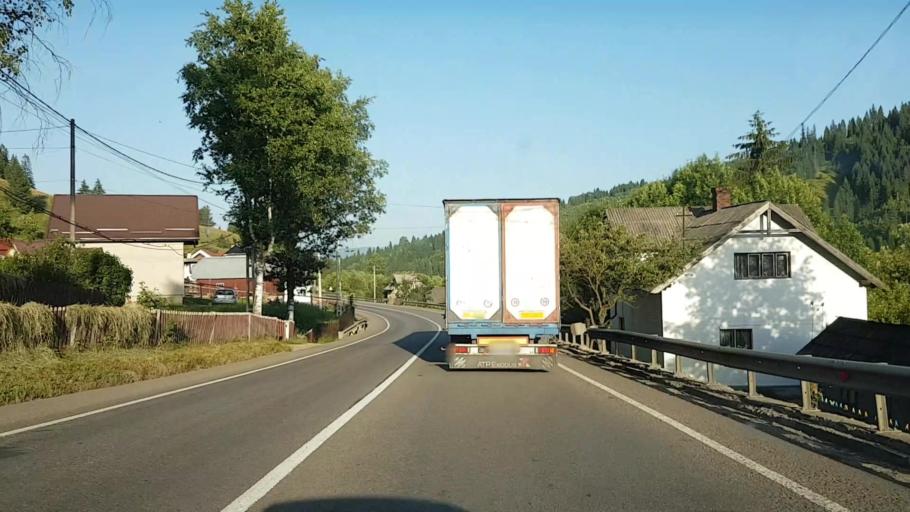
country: RO
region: Suceava
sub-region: Comuna Dorna Candrenilor
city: Dorna Candrenilor
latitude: 47.3573
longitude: 25.2758
